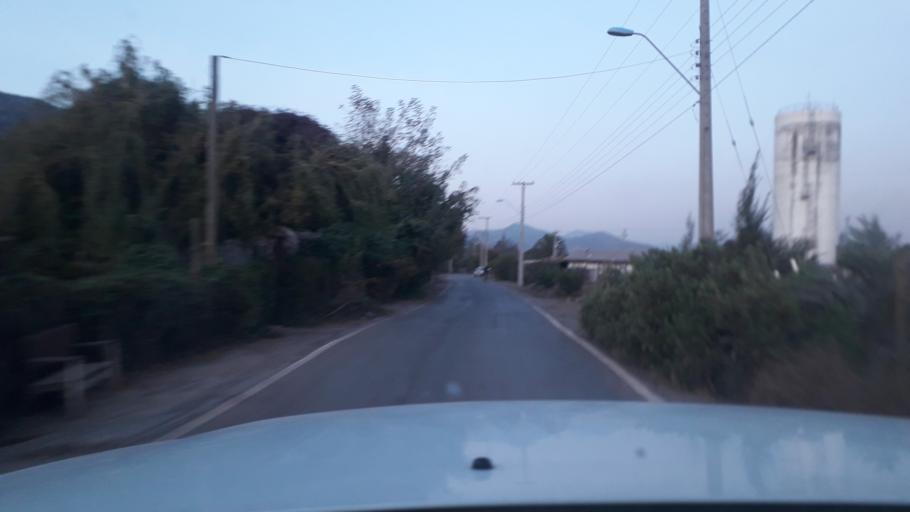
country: CL
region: Valparaiso
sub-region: Provincia de San Felipe
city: Llaillay
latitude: -32.8253
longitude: -71.0258
